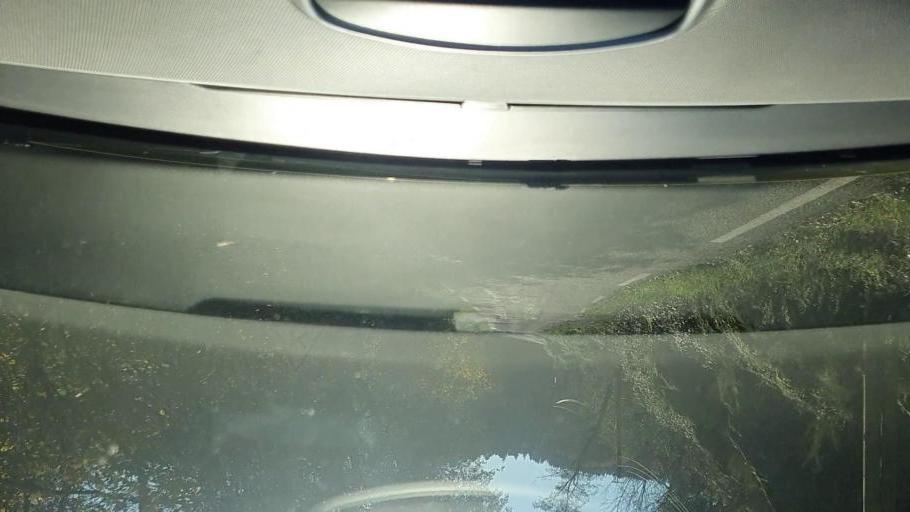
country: FR
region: Languedoc-Roussillon
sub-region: Departement du Gard
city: Lasalle
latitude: 44.0521
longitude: 3.8416
